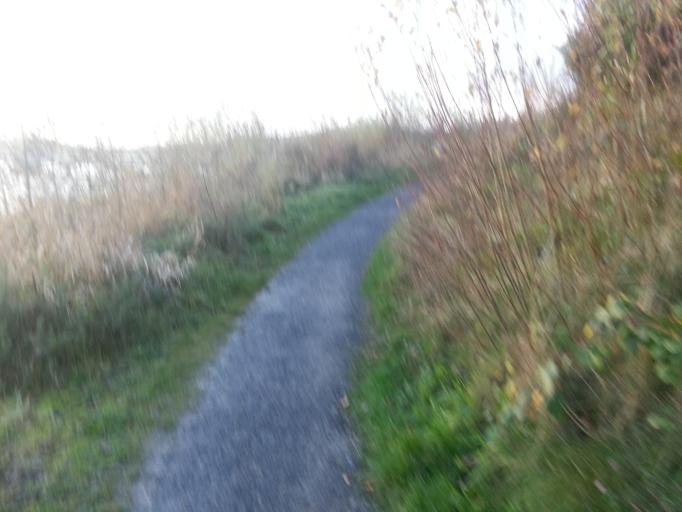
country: IE
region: Ulster
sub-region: County Monaghan
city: Clones
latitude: 54.2281
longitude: -7.2803
